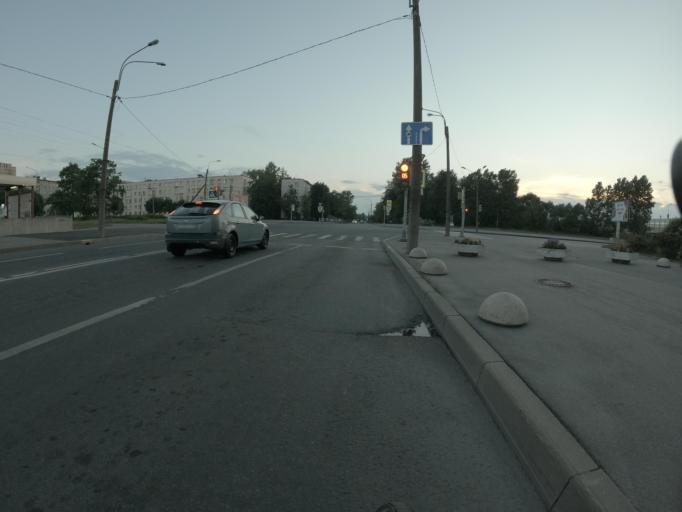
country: RU
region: St.-Petersburg
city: Avtovo
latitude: 59.8543
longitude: 30.2818
